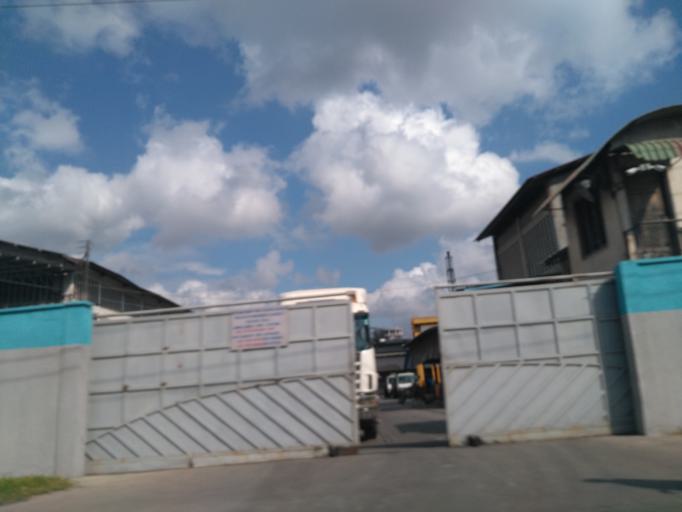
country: TZ
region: Dar es Salaam
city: Magomeni
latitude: -6.7641
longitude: 39.2357
